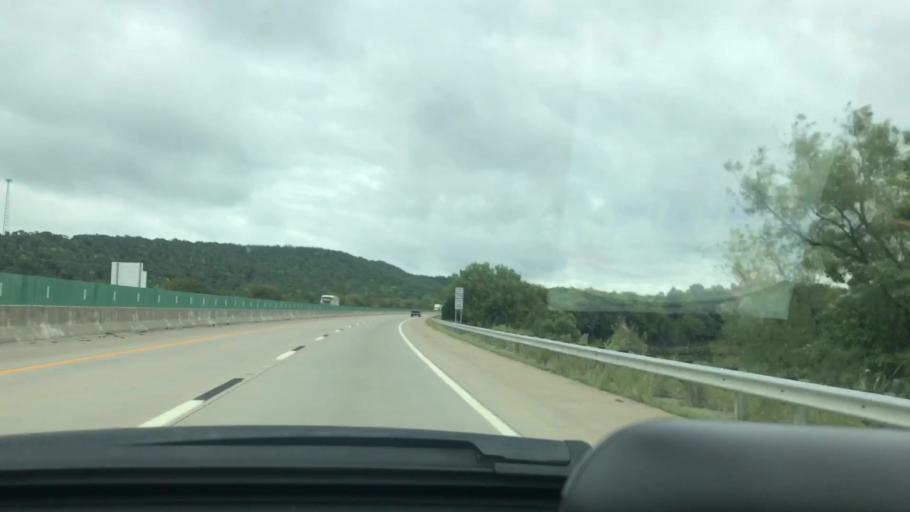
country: US
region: Oklahoma
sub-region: Pittsburg County
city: Krebs
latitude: 35.1091
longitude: -95.6932
